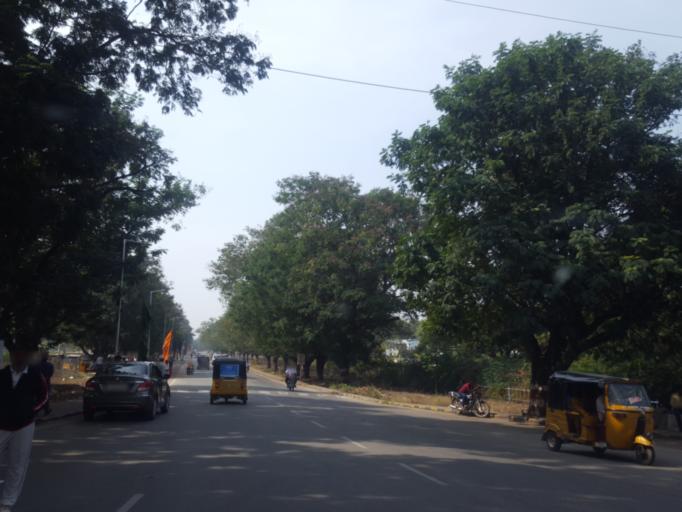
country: IN
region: Telangana
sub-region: Medak
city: Serilingampalle
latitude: 17.4946
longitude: 78.3150
